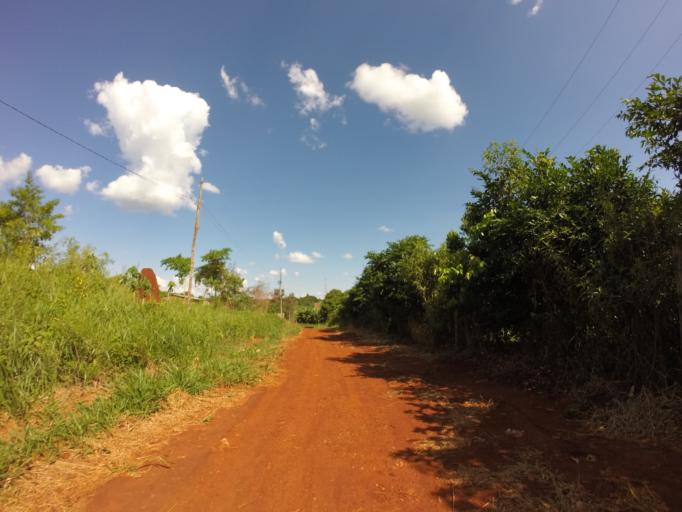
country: PY
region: Alto Parana
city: Ciudad del Este
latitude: -25.3774
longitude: -54.6647
